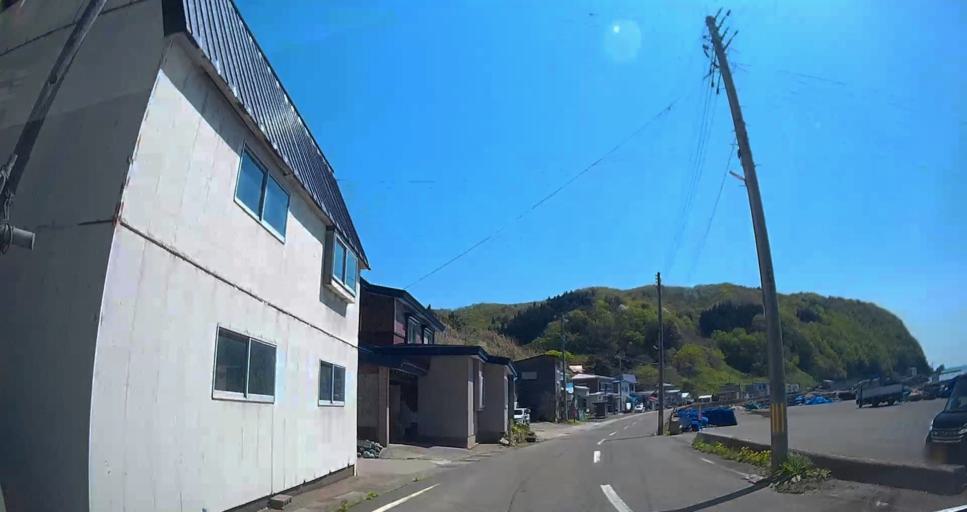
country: JP
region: Aomori
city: Aomori Shi
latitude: 41.1337
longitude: 140.7911
